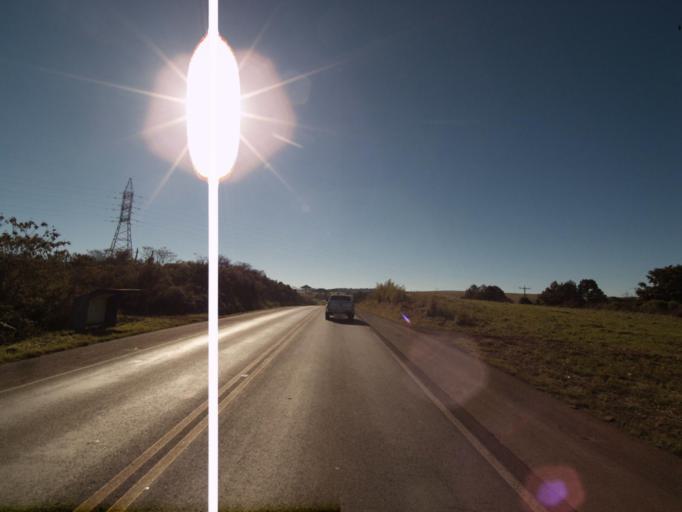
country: BR
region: Santa Catarina
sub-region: Concordia
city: Concordia
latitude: -26.9177
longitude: -51.9256
